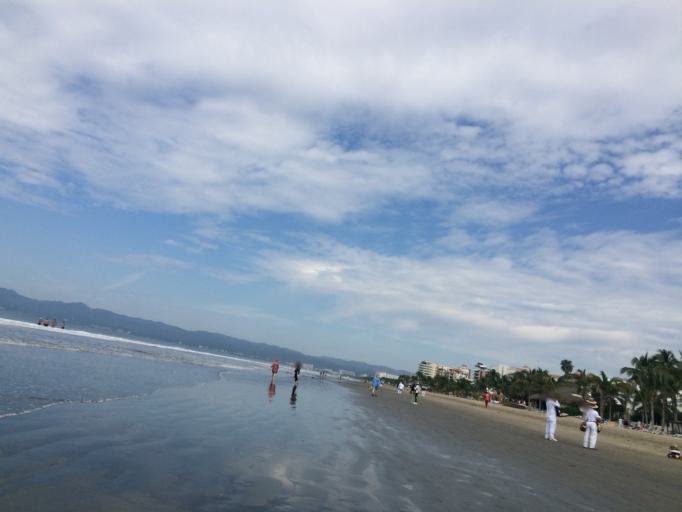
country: MX
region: Nayarit
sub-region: Bahia de Banderas
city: Las Jarretaderas
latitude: 20.6944
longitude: -105.2981
